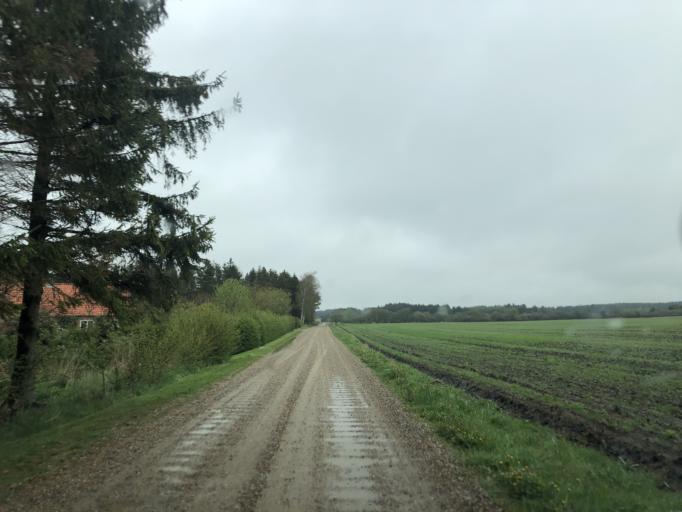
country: DK
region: Central Jutland
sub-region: Lemvig Kommune
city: Lemvig
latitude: 56.4417
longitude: 8.3745
